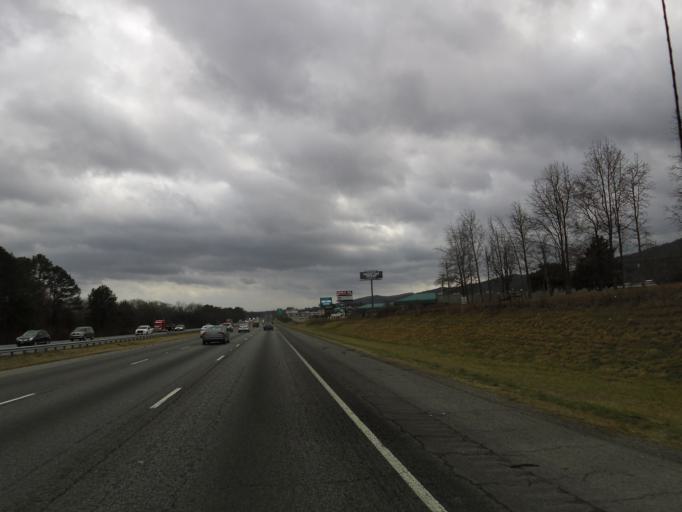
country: US
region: Georgia
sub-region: Whitfield County
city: Dalton
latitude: 34.6997
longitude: -85.0057
